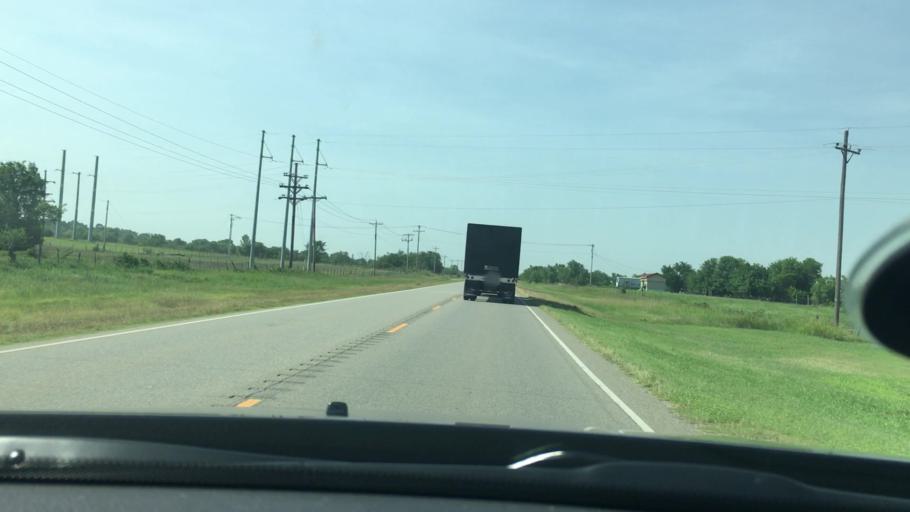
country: US
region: Oklahoma
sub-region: Coal County
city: Coalgate
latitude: 34.4862
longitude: -96.2186
